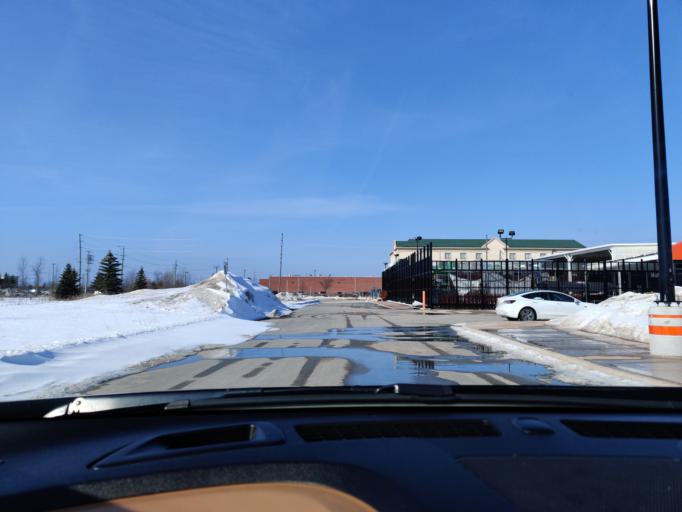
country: CA
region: Ontario
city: Collingwood
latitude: 44.4985
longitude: -80.2362
